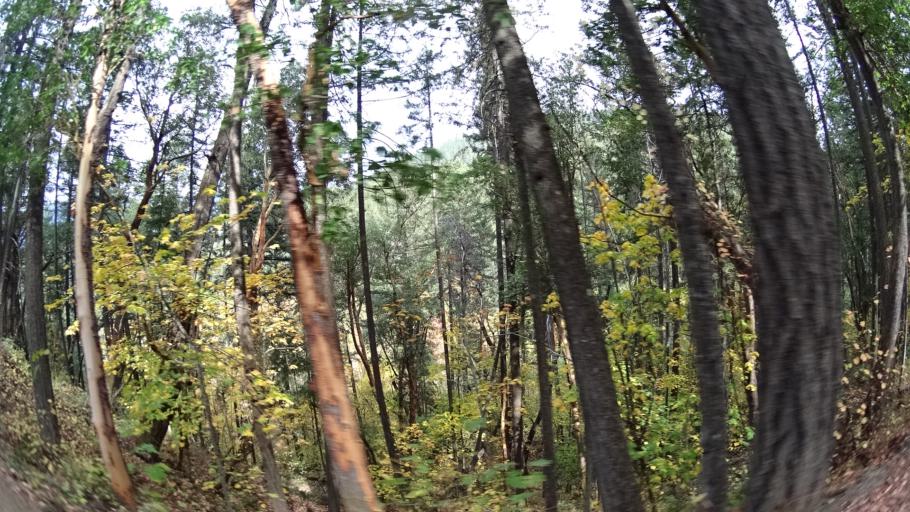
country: US
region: California
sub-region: Siskiyou County
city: Happy Camp
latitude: 41.7946
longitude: -123.3091
